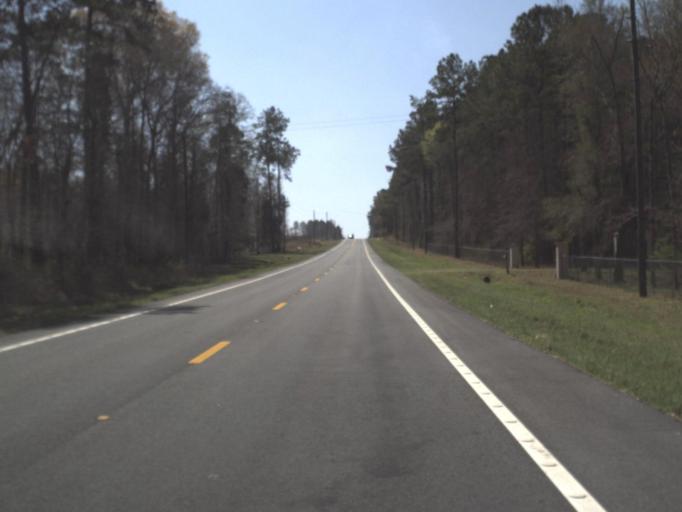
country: US
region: Florida
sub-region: Jefferson County
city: Monticello
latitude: 30.4653
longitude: -84.0195
